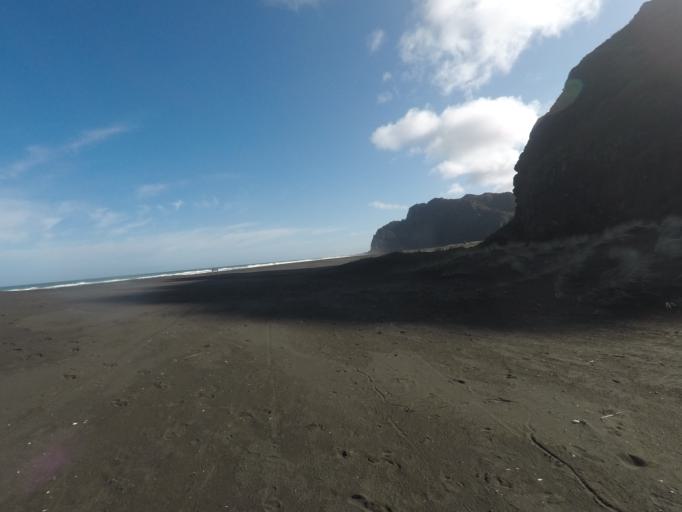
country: NZ
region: Auckland
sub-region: Auckland
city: Muriwai Beach
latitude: -36.9946
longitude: 174.4737
